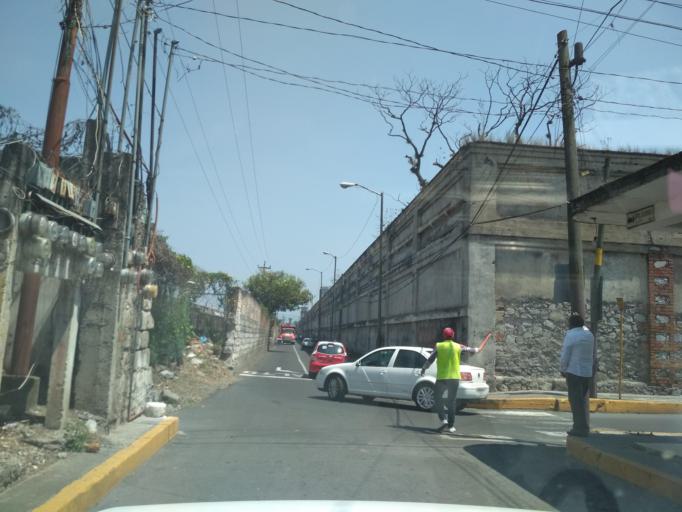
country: MX
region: Veracruz
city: Orizaba
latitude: 18.8376
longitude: -97.1075
